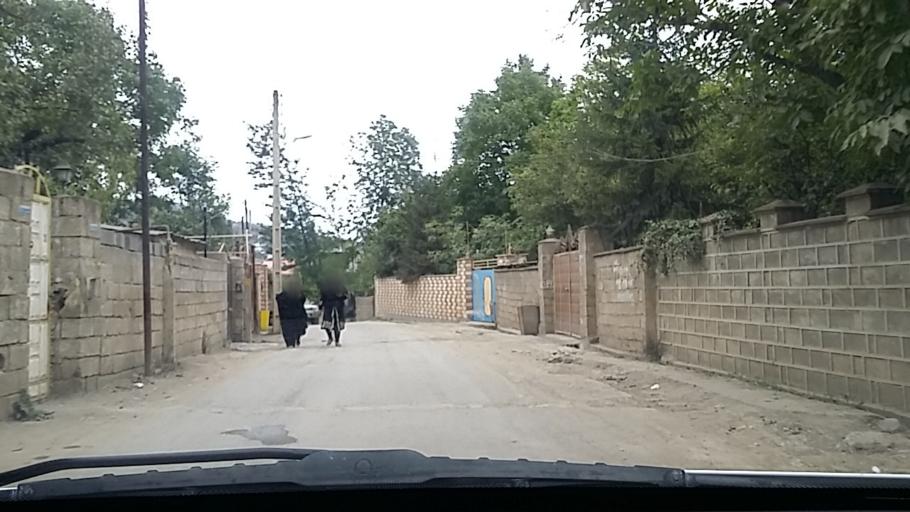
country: IR
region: Mazandaran
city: `Abbasabad
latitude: 36.5125
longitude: 51.1632
